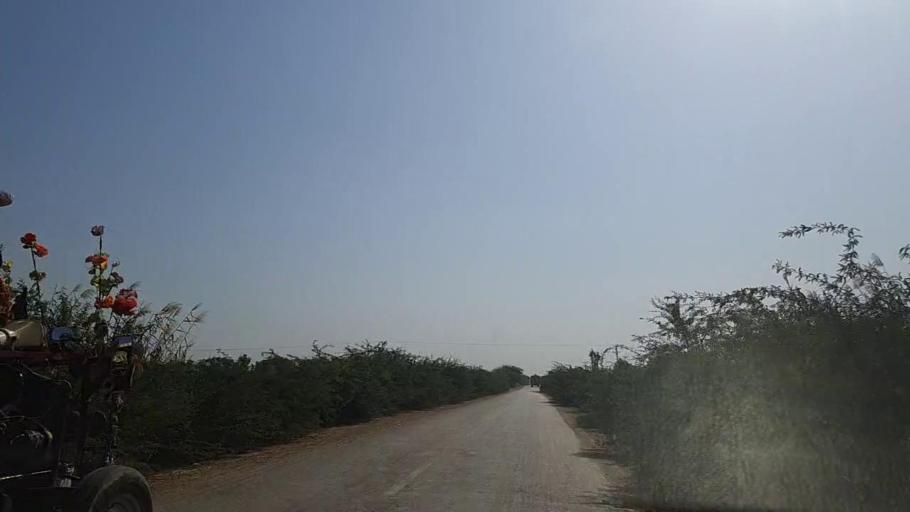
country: PK
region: Sindh
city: Mirpur Batoro
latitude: 24.6041
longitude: 68.2953
